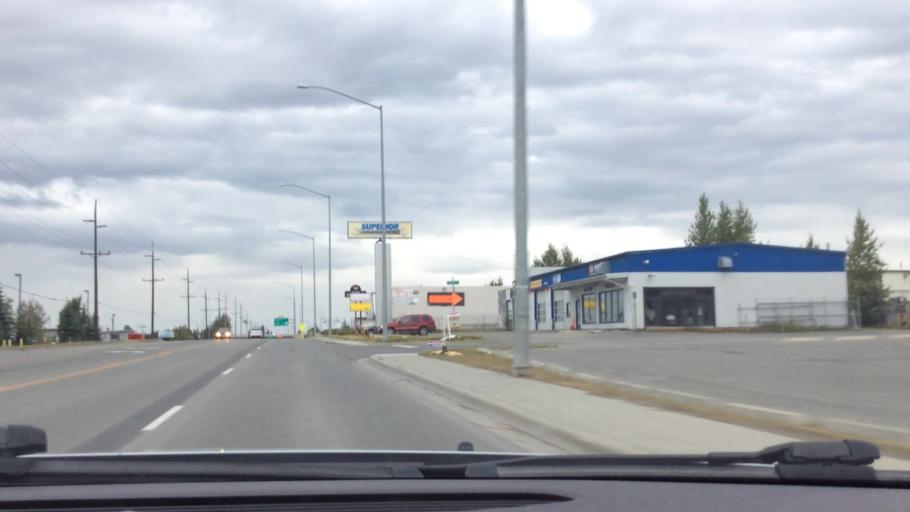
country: US
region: Alaska
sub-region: Anchorage Municipality
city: Anchorage
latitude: 61.1665
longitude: -149.8478
